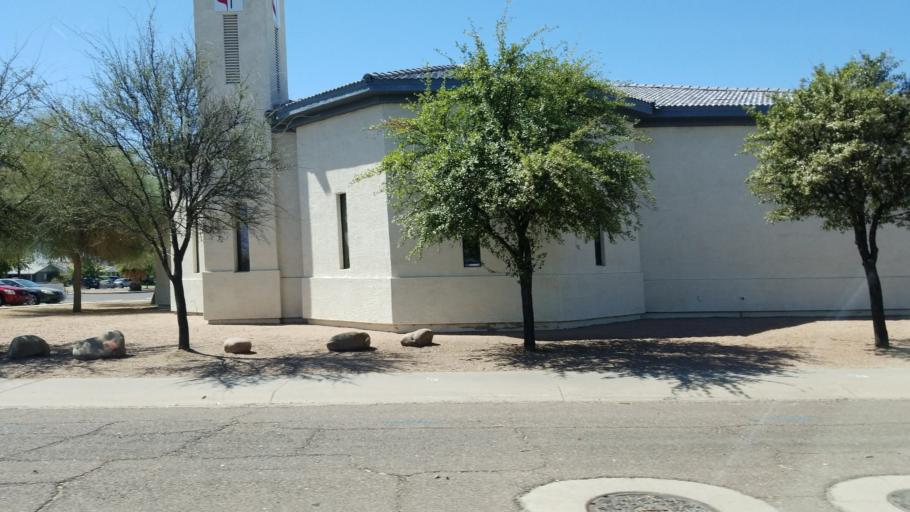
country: US
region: Arizona
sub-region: Maricopa County
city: Tolleson
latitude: 33.4944
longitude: -112.2305
